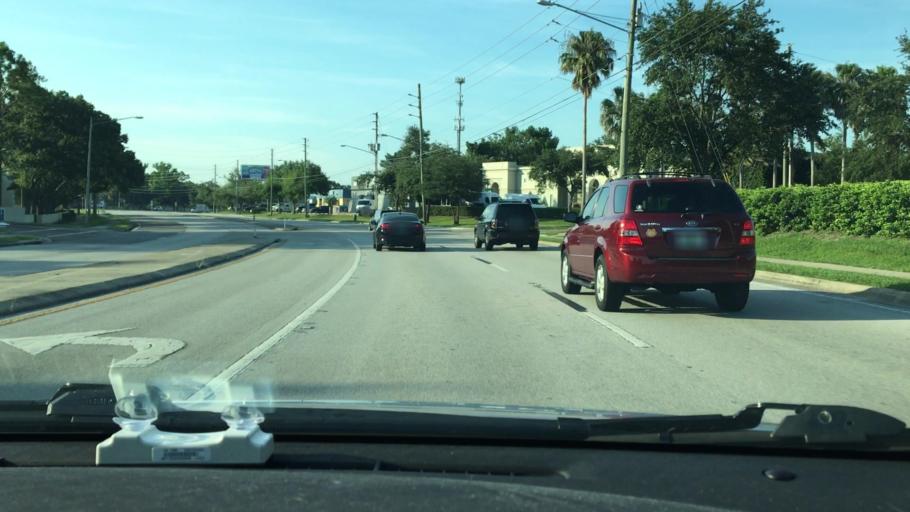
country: US
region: Florida
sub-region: Seminole County
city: Goldenrod
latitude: 28.6070
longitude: -81.2885
